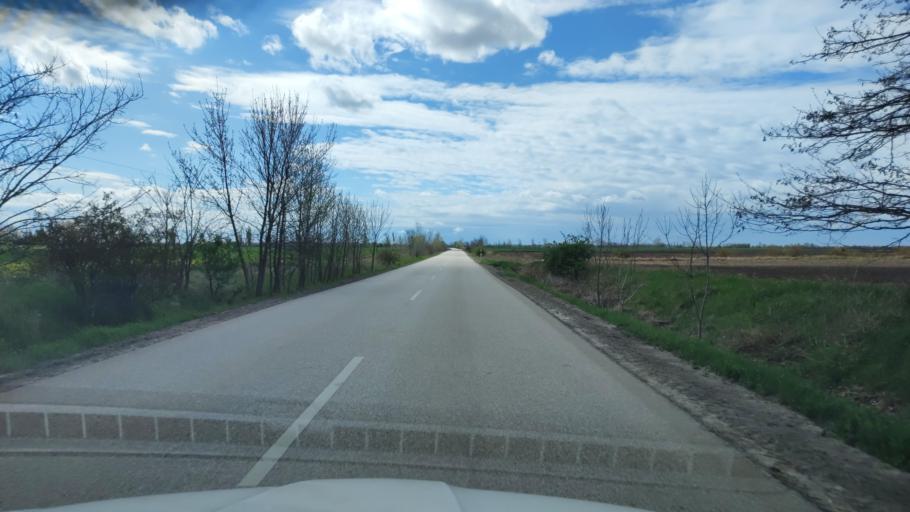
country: HU
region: Pest
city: Abony
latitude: 47.1223
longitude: 20.0142
